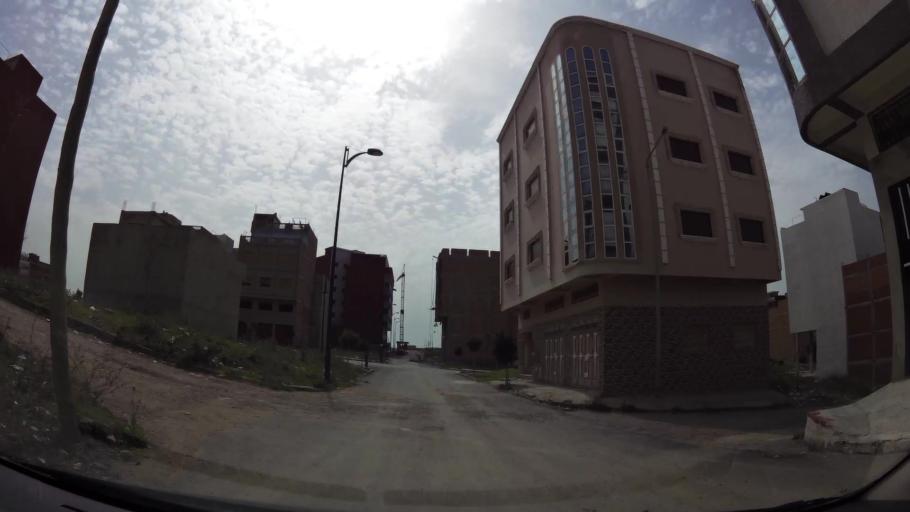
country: MA
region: Tanger-Tetouan
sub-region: Tanger-Assilah
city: Tangier
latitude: 35.7405
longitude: -5.8371
